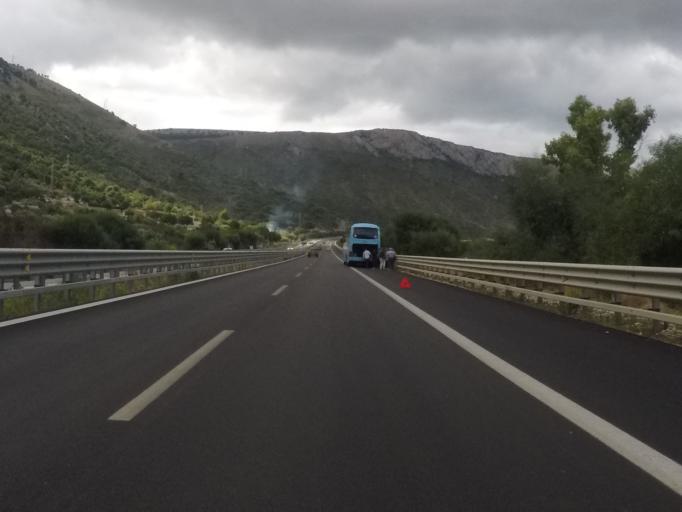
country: IT
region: Sicily
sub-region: Palermo
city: Cinisi
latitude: 38.1446
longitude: 13.1065
